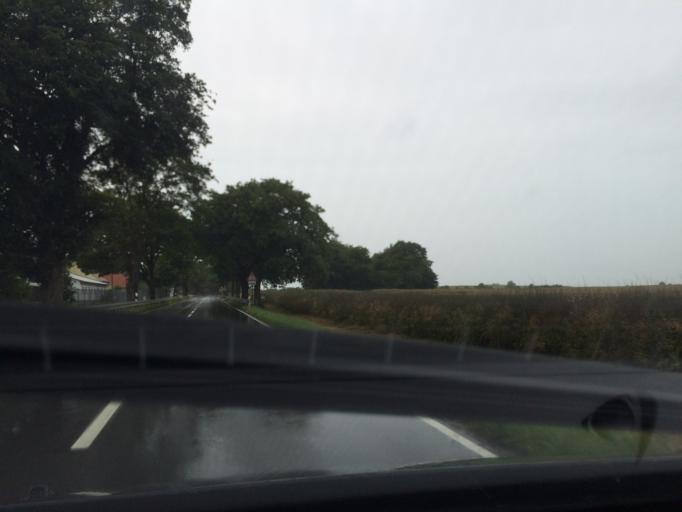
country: DE
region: Mecklenburg-Vorpommern
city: Kramerhof
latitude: 54.3391
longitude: 13.0555
